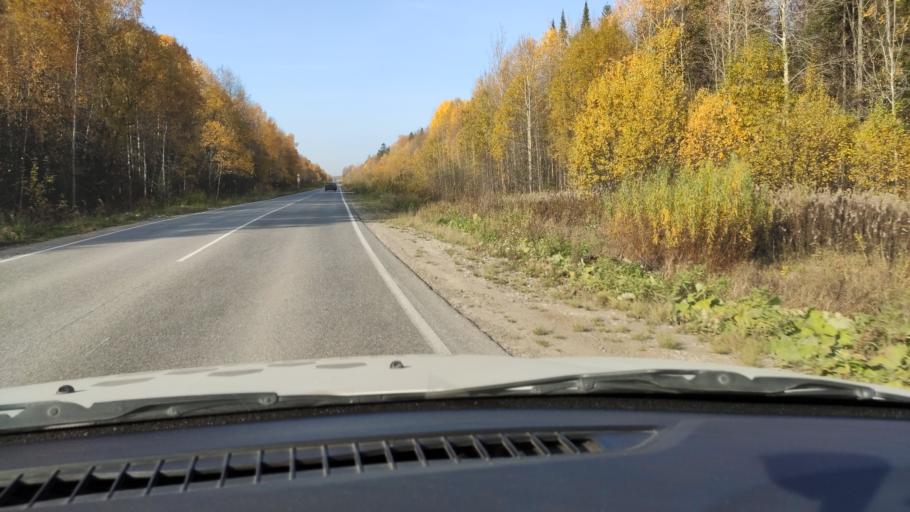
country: RU
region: Perm
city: Novyye Lyady
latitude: 58.0238
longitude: 56.6392
